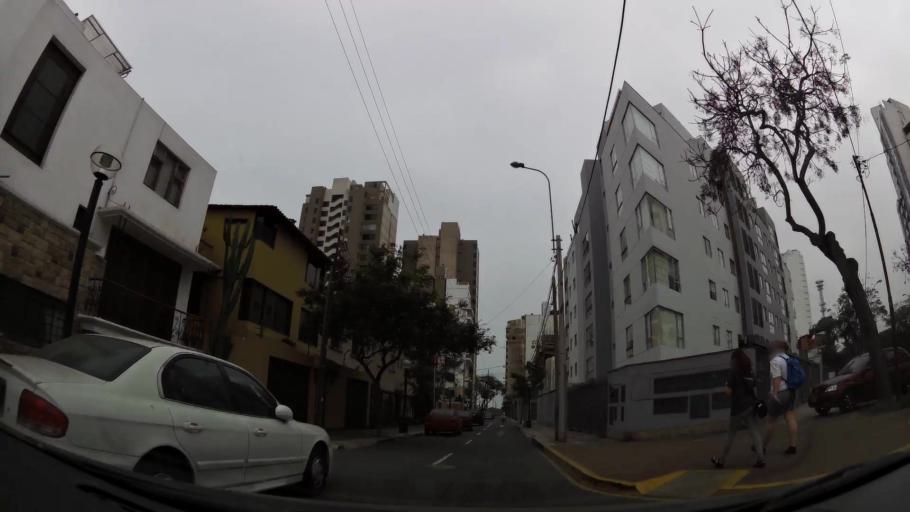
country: PE
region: Lima
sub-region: Lima
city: San Isidro
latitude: -12.1201
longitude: -77.0418
